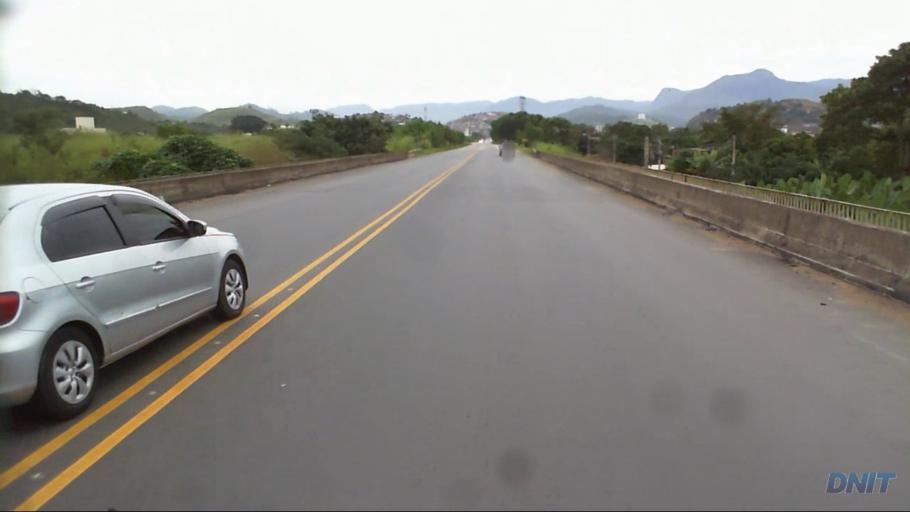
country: BR
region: Minas Gerais
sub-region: Coronel Fabriciano
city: Coronel Fabriciano
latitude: -19.5316
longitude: -42.6024
